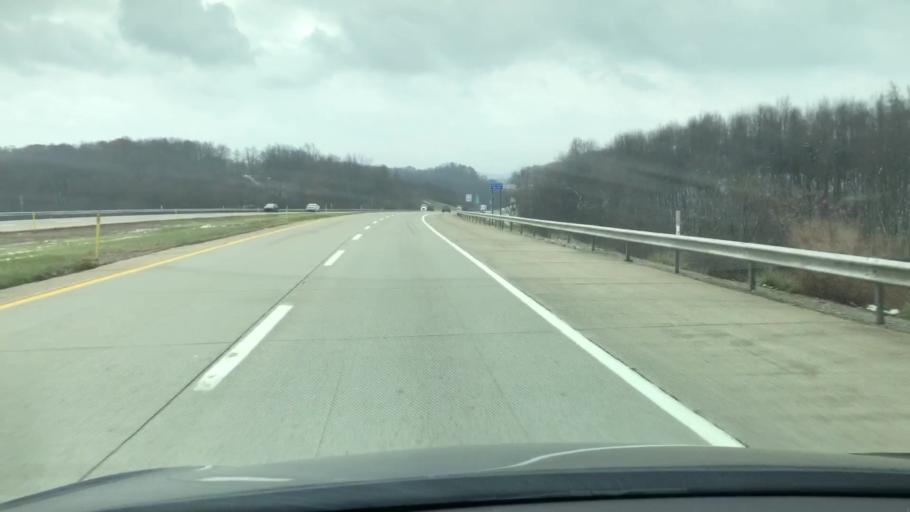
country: US
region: Pennsylvania
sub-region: Westmoreland County
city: Youngwood
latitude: 40.2641
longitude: -79.6144
